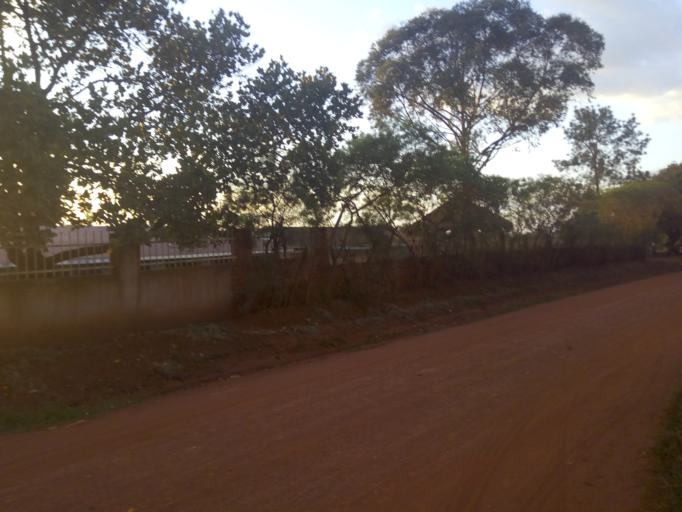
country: UG
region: Western Region
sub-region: Masindi District
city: Masindi
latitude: 1.6727
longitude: 31.7133
